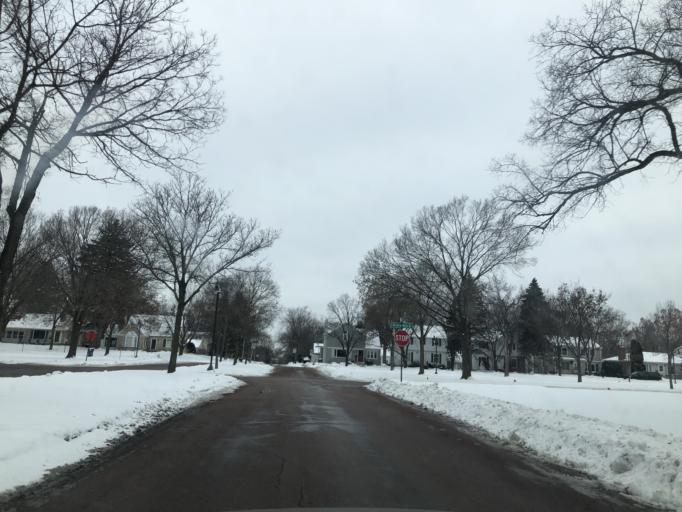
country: US
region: Minnesota
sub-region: Hennepin County
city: Robbinsdale
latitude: 45.0242
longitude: -93.3187
